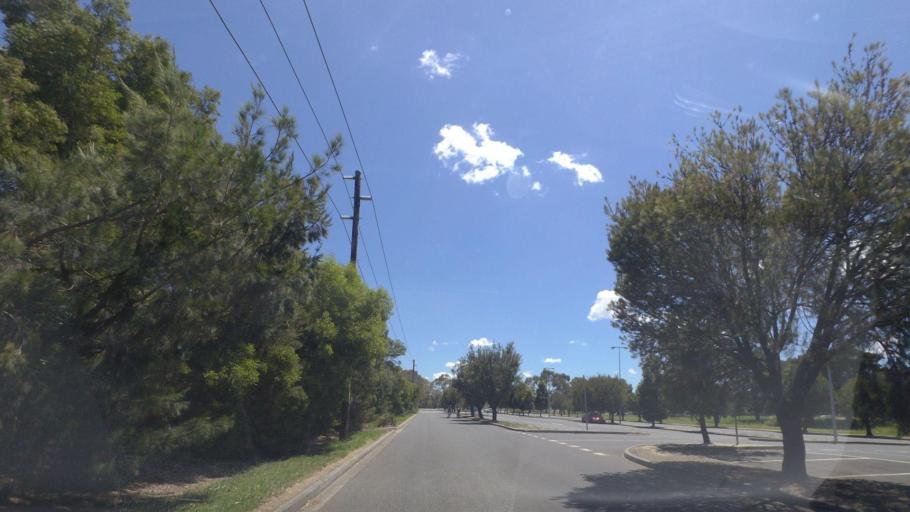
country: AU
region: Victoria
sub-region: Knox
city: Knoxfield
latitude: -37.8984
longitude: 145.2571
